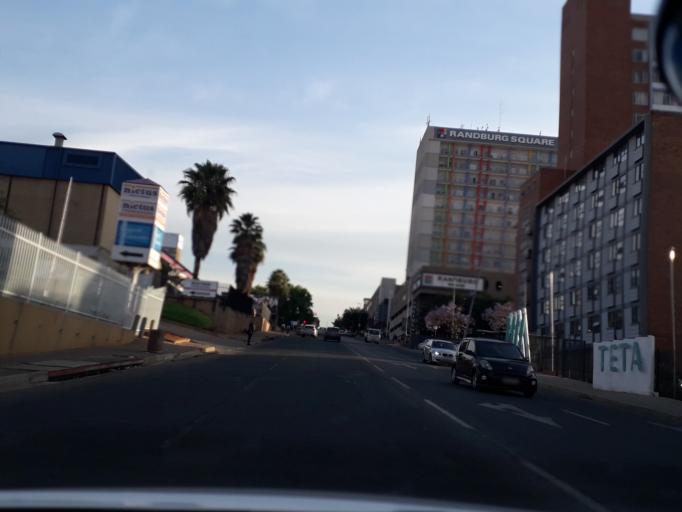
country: ZA
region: Gauteng
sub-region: City of Johannesburg Metropolitan Municipality
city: Johannesburg
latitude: -26.0902
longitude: 28.0047
